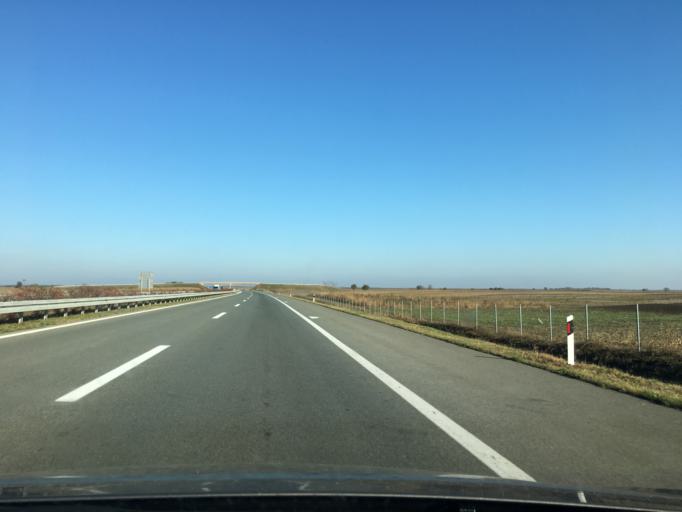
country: RS
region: Autonomna Pokrajina Vojvodina
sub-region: Severnobacki Okrug
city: Mali Igos
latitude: 45.6610
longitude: 19.7262
